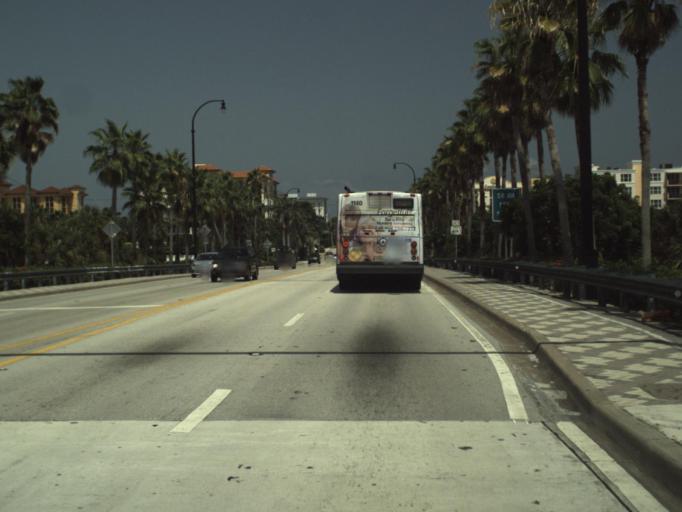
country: US
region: Florida
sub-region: Broward County
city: Deerfield Beach
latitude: 26.3144
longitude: -80.0803
